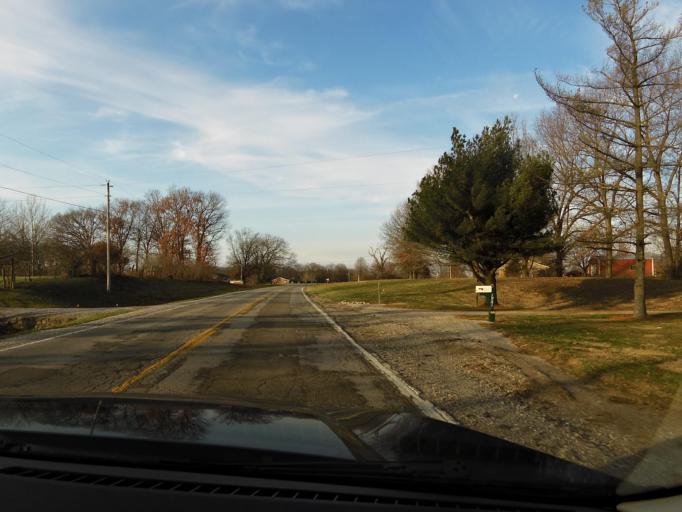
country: US
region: Illinois
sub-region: Bond County
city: Greenville
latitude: 38.9195
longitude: -89.2601
